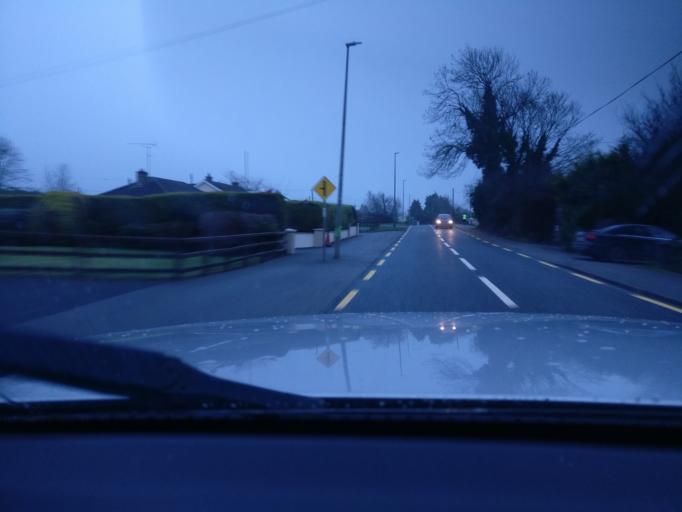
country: IE
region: Leinster
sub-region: An Iarmhi
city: Rathwire
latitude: 53.6132
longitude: -7.0821
